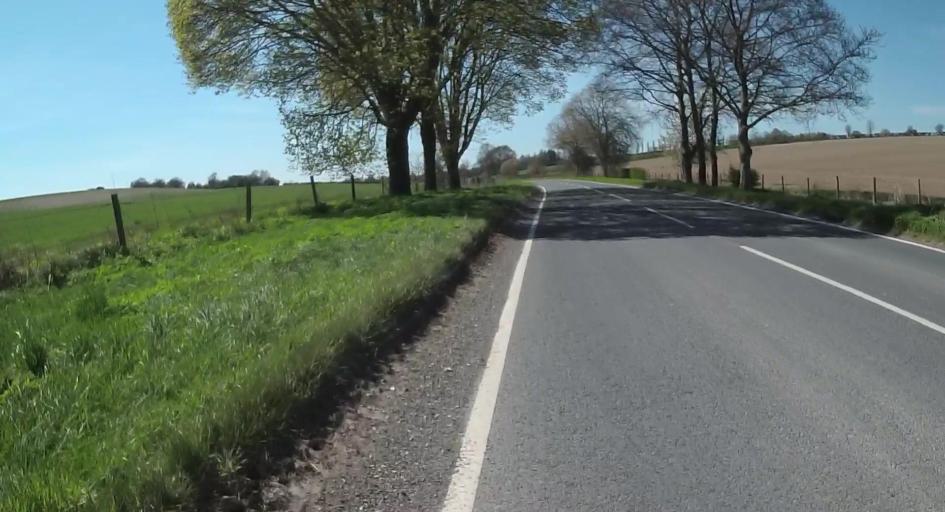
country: GB
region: England
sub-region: Hampshire
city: Chandlers Ford
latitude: 51.0947
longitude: -1.4220
